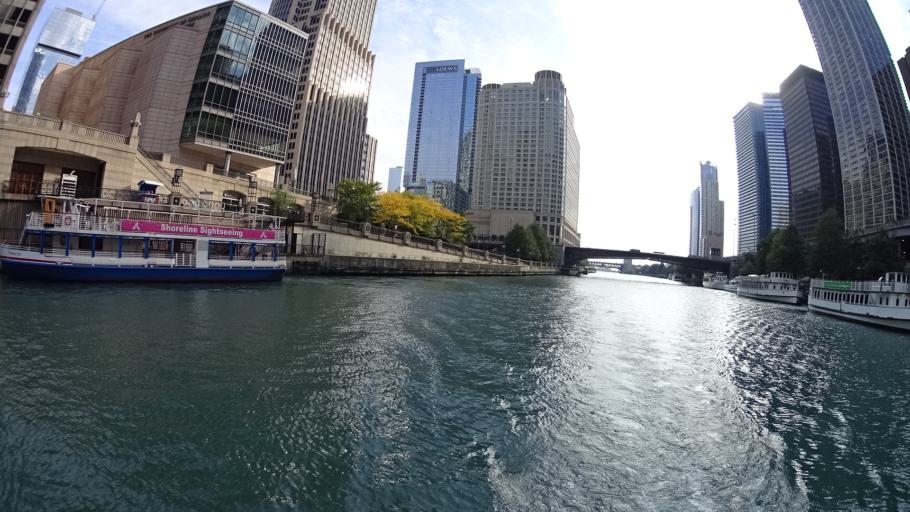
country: US
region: Illinois
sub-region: Cook County
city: Chicago
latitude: 41.8889
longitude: -87.6227
